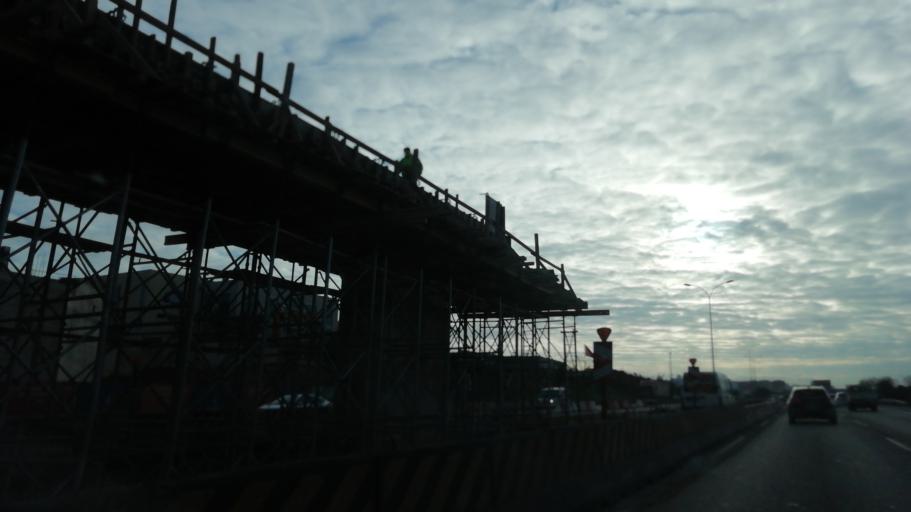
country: TR
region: Kocaeli
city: Balcik
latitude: 40.8830
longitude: 29.3785
